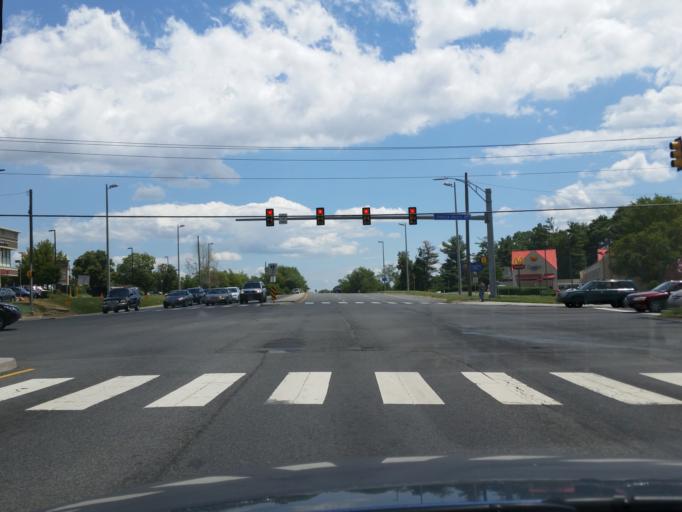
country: US
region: Virginia
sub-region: Fairfax County
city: Seven Corners
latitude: 38.8687
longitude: -77.1471
